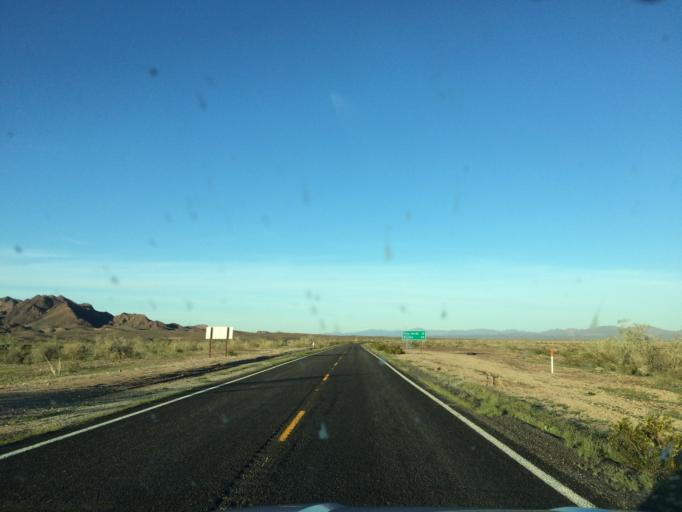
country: US
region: California
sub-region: Riverside County
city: Mesa Verde
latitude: 33.2711
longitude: -114.7948
